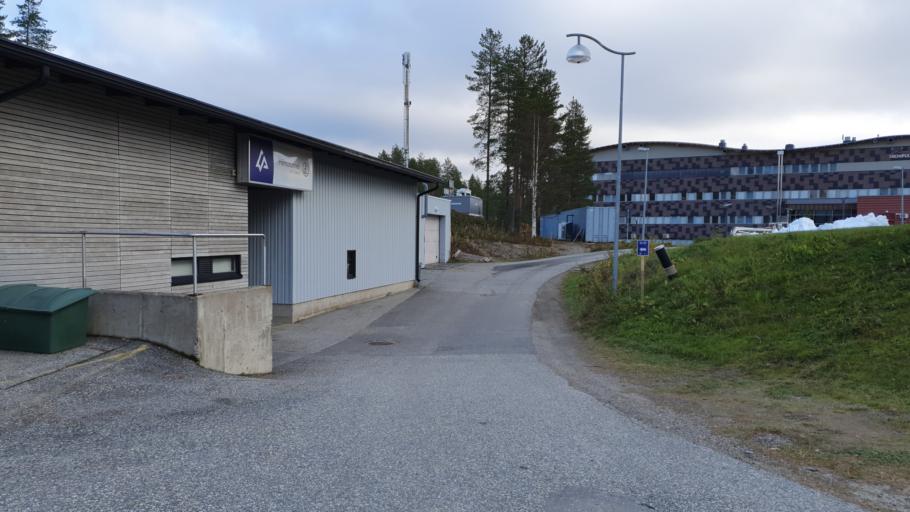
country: FI
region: Kainuu
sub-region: Kajaani
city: Vuokatti
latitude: 64.1405
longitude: 28.2917
